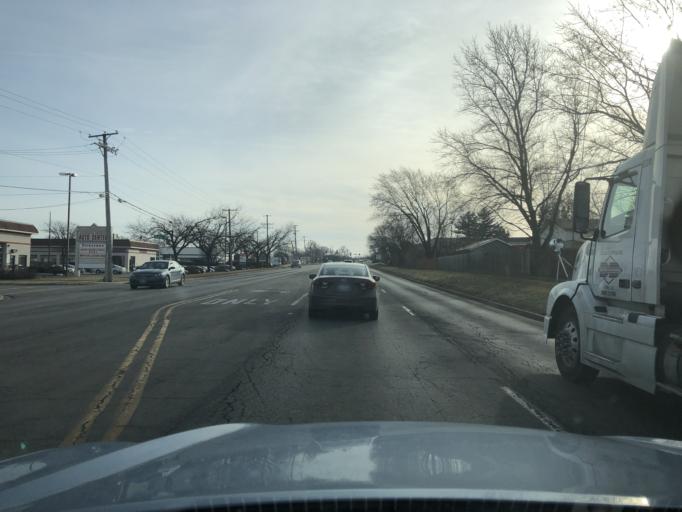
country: US
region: Illinois
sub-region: DuPage County
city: Bloomingdale
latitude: 41.9337
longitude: -88.0801
